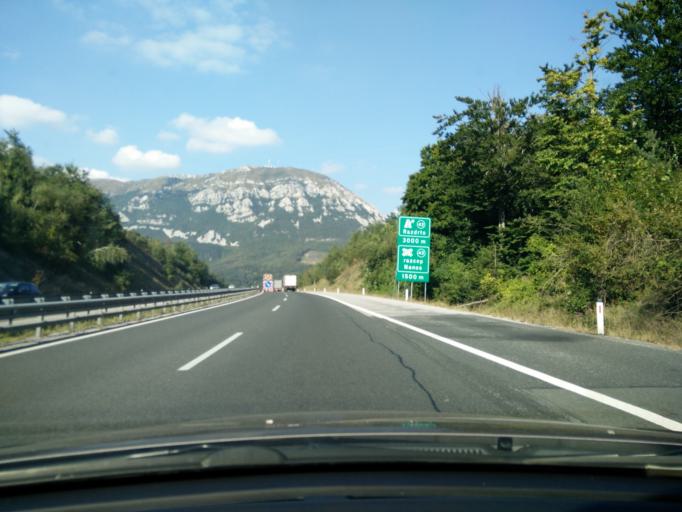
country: SI
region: Divaca
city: Divaca
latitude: 45.7463
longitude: 14.0415
